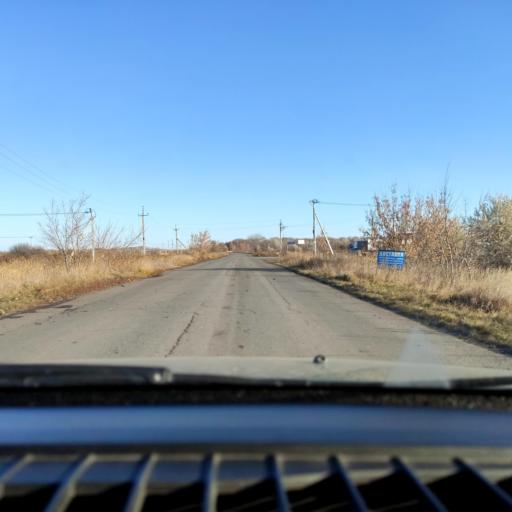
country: RU
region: Samara
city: Tol'yatti
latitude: 53.6441
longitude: 49.3167
